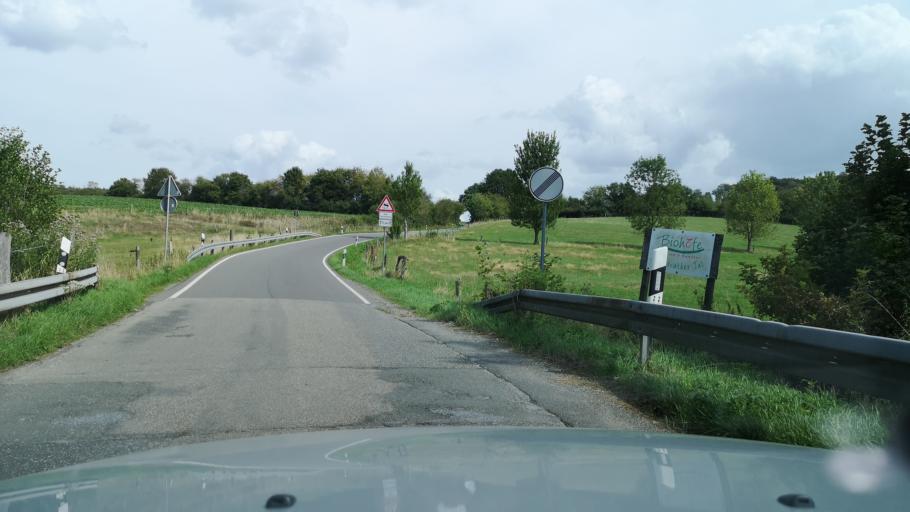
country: DE
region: North Rhine-Westphalia
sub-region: Regierungsbezirk Dusseldorf
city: Wuppertal
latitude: 51.3306
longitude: 7.1388
